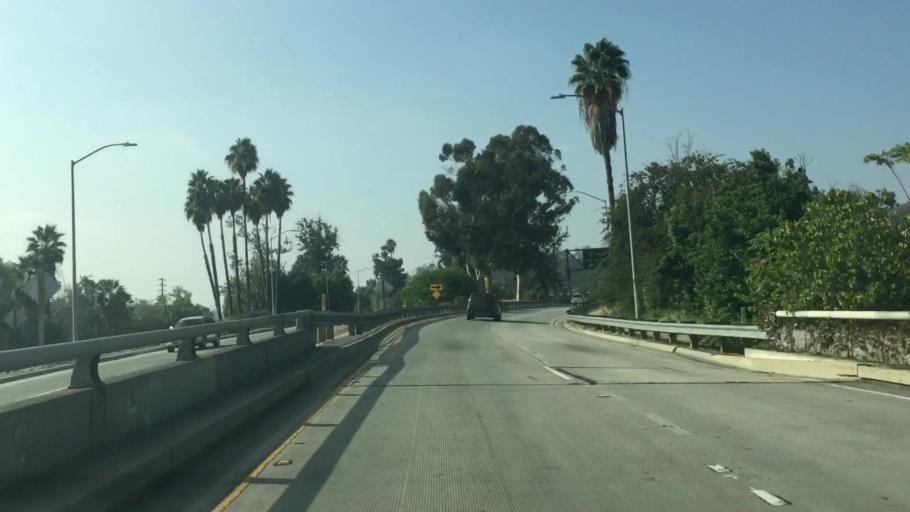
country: US
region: California
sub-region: Los Angeles County
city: Los Angeles
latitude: 34.0838
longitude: -118.2198
